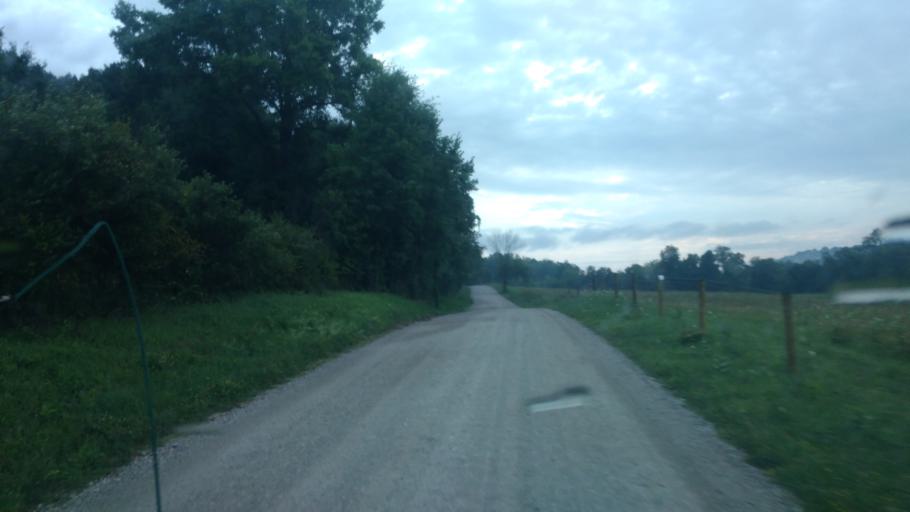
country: US
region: Ohio
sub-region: Belmont County
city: Barnesville
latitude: 40.0254
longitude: -81.3546
